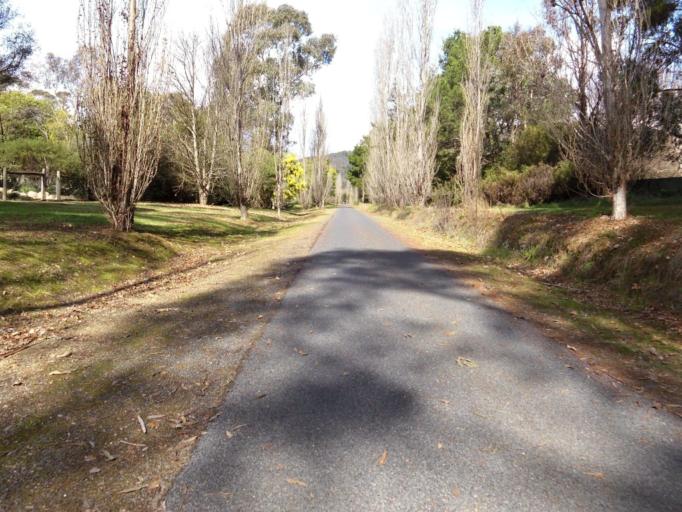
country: AU
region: Victoria
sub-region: Alpine
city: Mount Beauty
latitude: -36.7198
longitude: 146.9447
